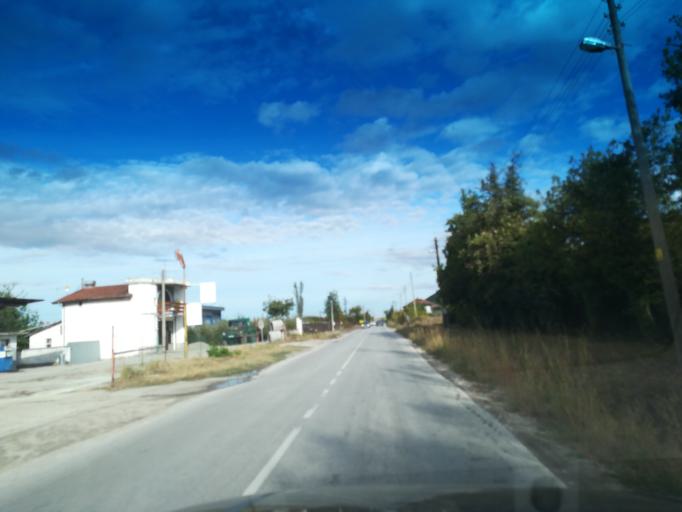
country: BG
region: Pazardzhik
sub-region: Obshtina Bratsigovo
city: Bratsigovo
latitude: 42.0642
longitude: 24.3673
